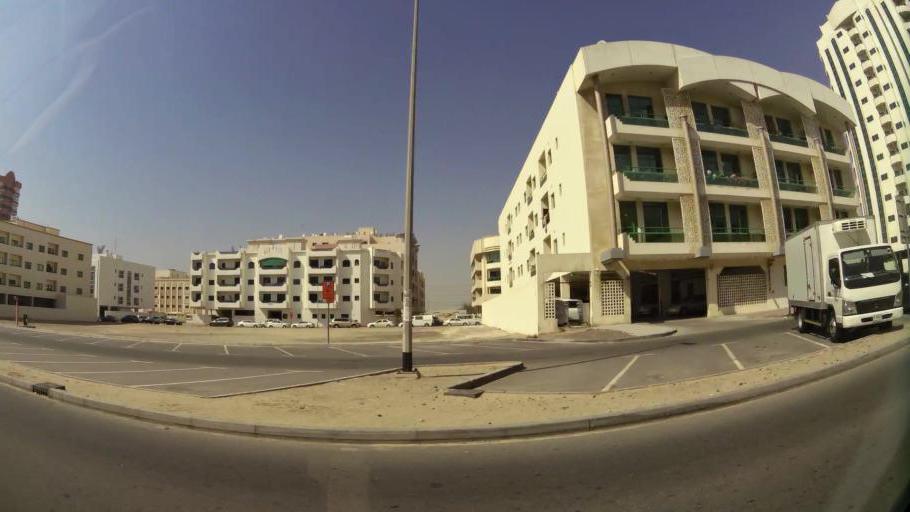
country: AE
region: Ash Shariqah
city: Sharjah
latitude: 25.2750
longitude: 55.3795
